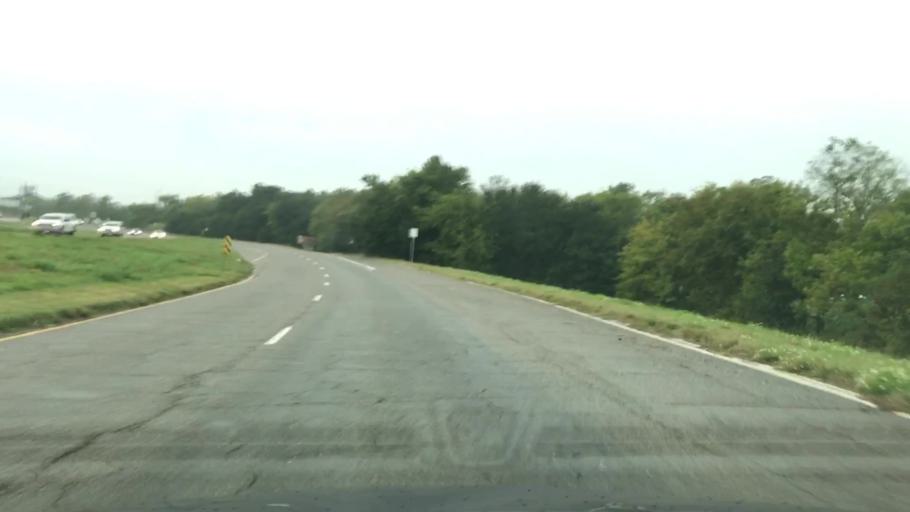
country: US
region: Louisiana
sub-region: Saint Charles Parish
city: Des Allemands
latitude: 29.8217
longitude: -90.4818
